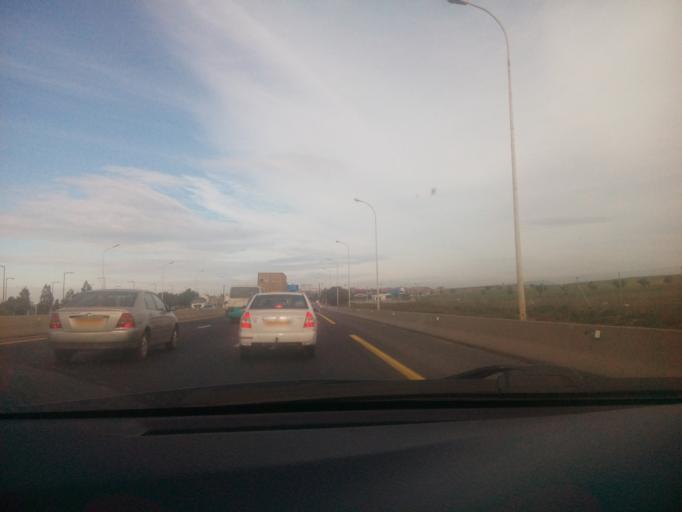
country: DZ
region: Oran
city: Es Senia
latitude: 35.5926
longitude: -0.5720
